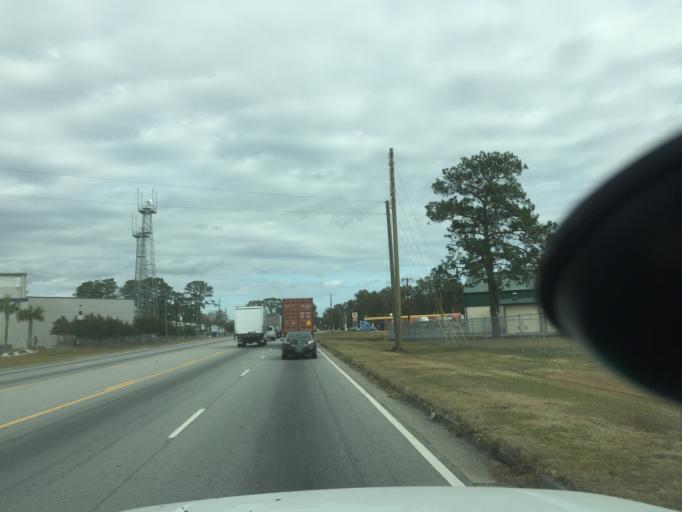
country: US
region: Georgia
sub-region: Chatham County
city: Garden City
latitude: 32.1135
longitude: -81.1937
